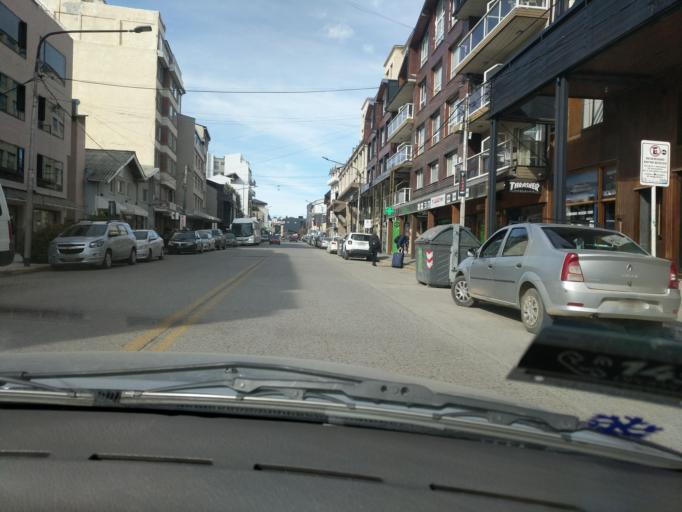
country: AR
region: Rio Negro
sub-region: Departamento de Bariloche
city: San Carlos de Bariloche
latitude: -41.1337
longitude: -71.3163
